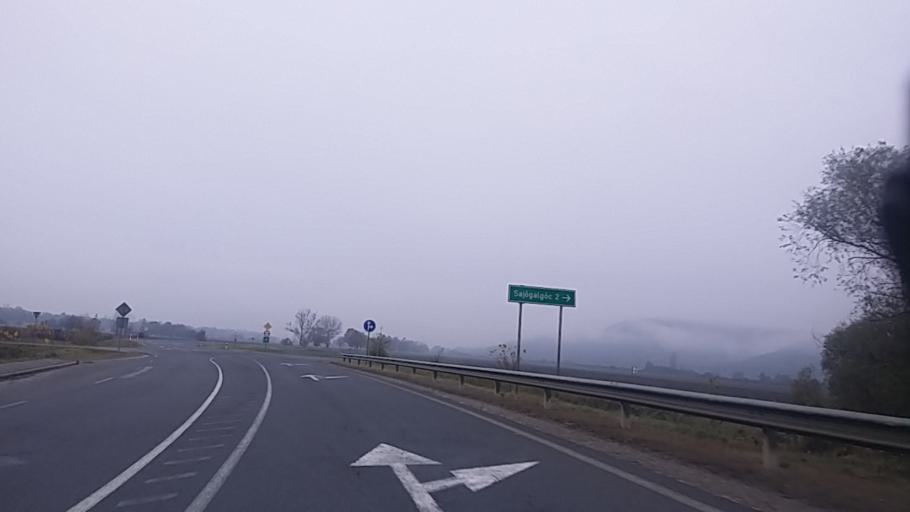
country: HU
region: Borsod-Abauj-Zemplen
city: Sajokaza
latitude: 48.2751
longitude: 20.5263
